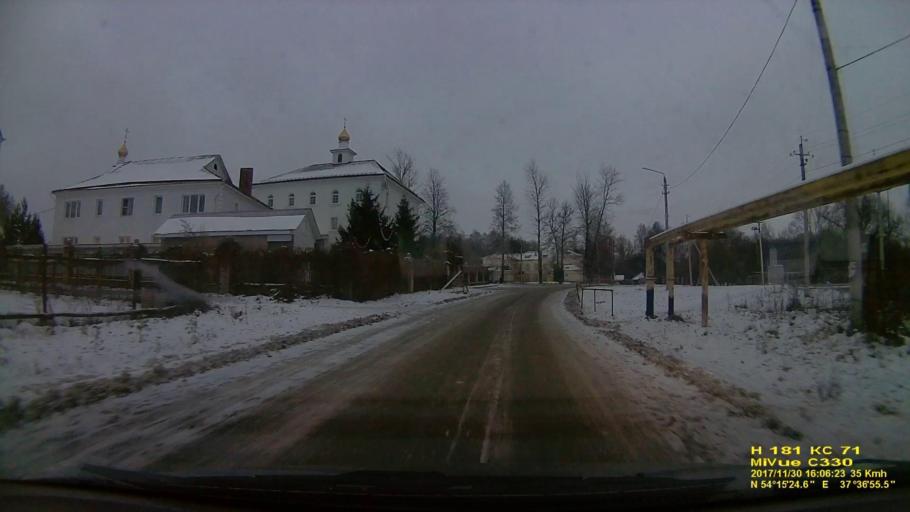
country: RU
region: Tula
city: Gorelki
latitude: 54.2567
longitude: 37.6154
